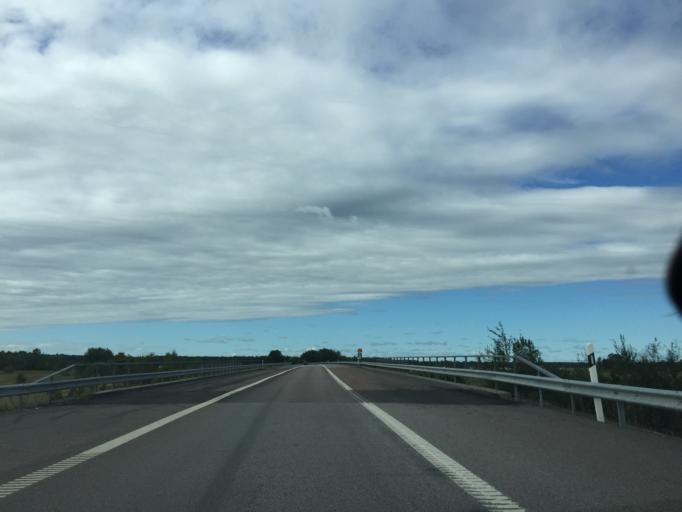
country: SE
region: Vaestmanland
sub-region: Arboga Kommun
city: Arboga
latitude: 59.4300
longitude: 15.8942
